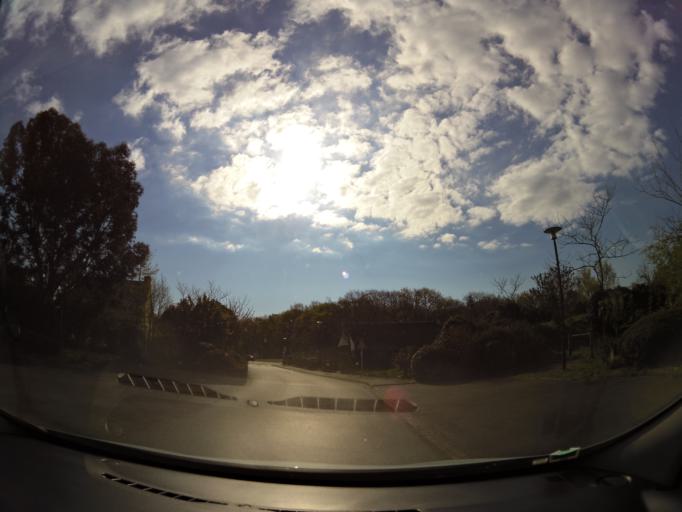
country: FR
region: Brittany
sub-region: Departement d'Ille-et-Vilaine
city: Laille
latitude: 47.9750
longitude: -1.7215
